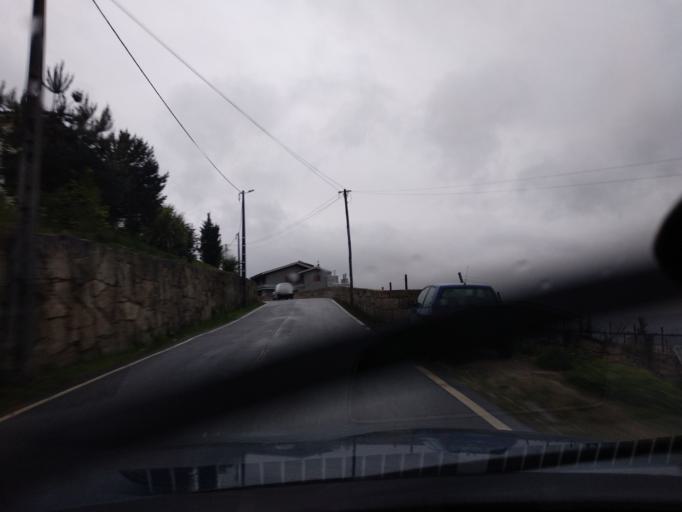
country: PT
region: Porto
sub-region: Penafiel
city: Penafiel
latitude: 41.1875
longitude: -8.2893
